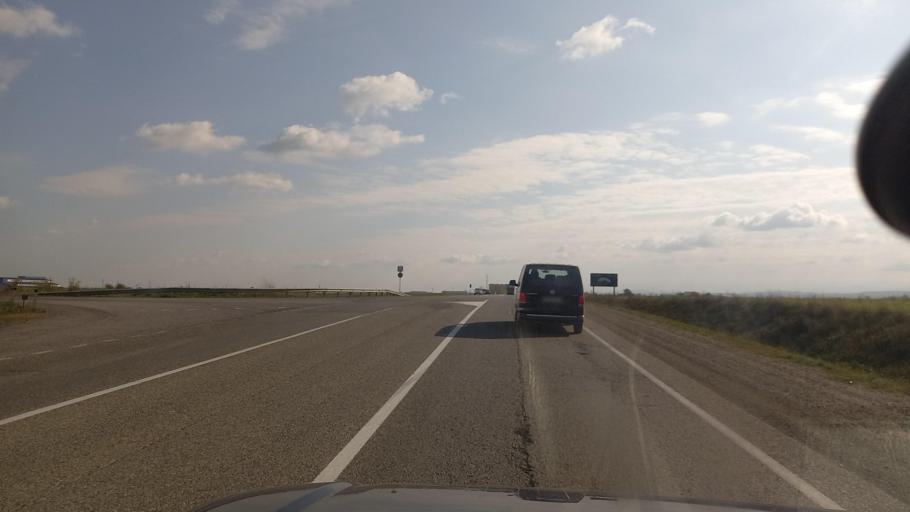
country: RU
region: Krasnodarskiy
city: Abinsk
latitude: 44.8739
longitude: 38.1146
